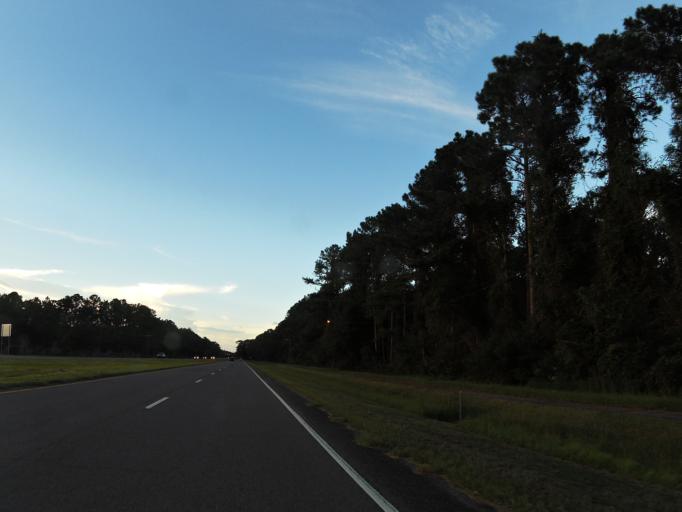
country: US
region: Georgia
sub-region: Camden County
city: Kings Bay Base
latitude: 30.7851
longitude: -81.5766
